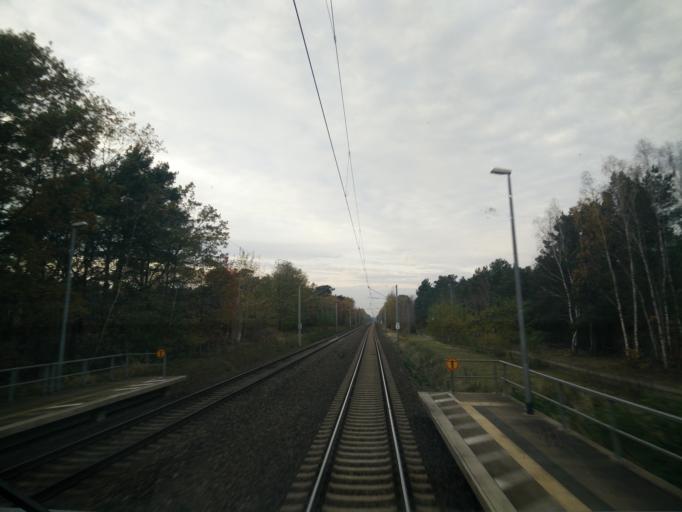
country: DE
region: Brandenburg
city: Kasel-Golzig
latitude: 51.9918
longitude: 13.7764
